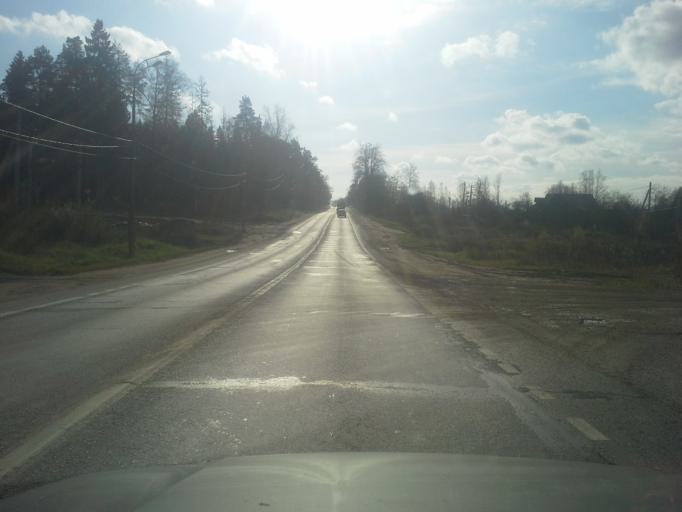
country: RU
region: Moskovskaya
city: Bol'shiye Vyazemy
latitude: 55.6589
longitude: 36.9676
